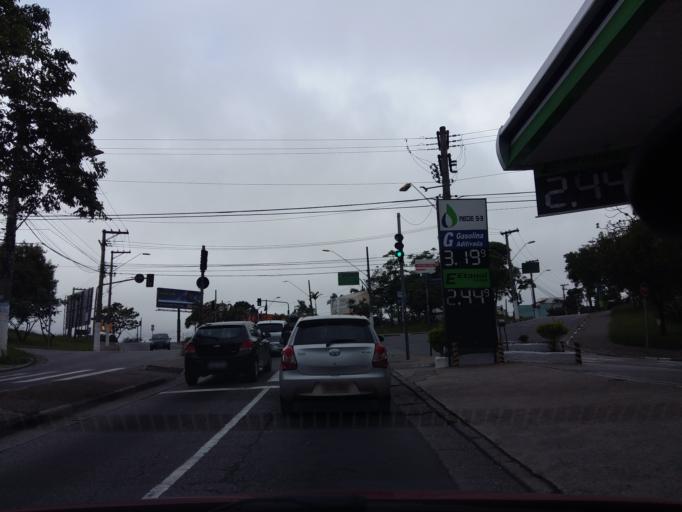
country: BR
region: Sao Paulo
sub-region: Santo Andre
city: Santo Andre
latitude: -23.6623
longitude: -46.5470
